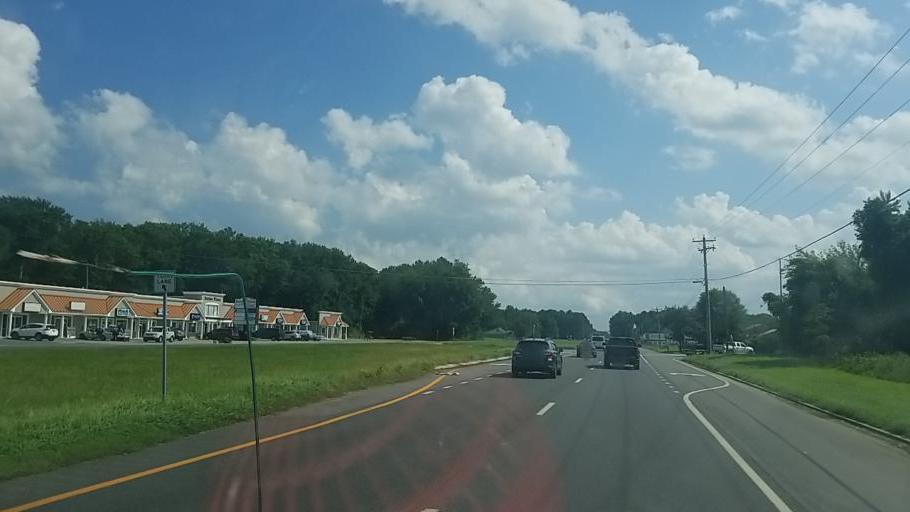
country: US
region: Delaware
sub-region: Sussex County
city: Selbyville
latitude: 38.5126
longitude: -75.2387
